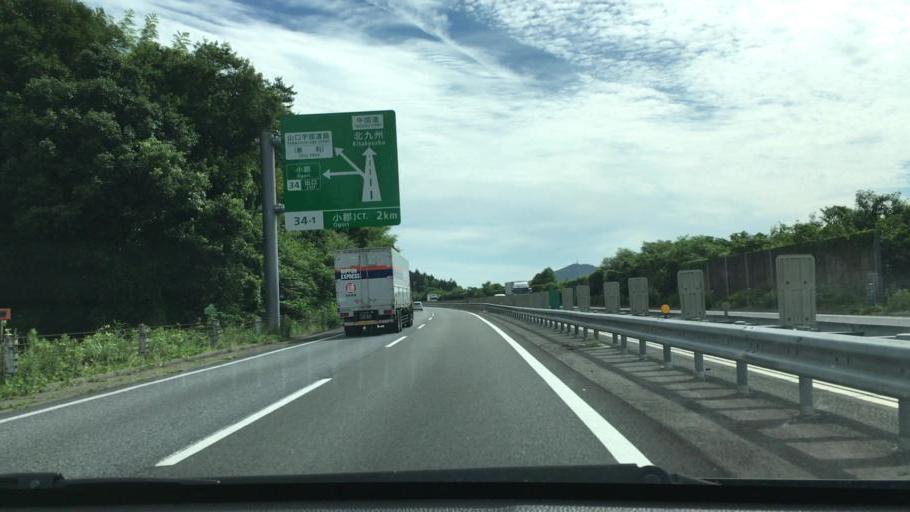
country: JP
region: Yamaguchi
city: Ogori-shimogo
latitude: 34.1302
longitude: 131.4239
